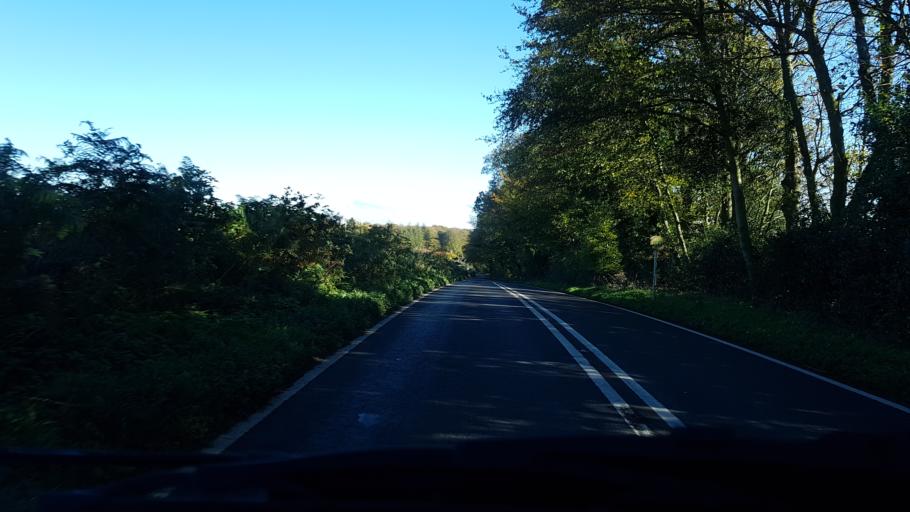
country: GB
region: England
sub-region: Surrey
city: Dorking
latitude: 51.2153
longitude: -0.3953
